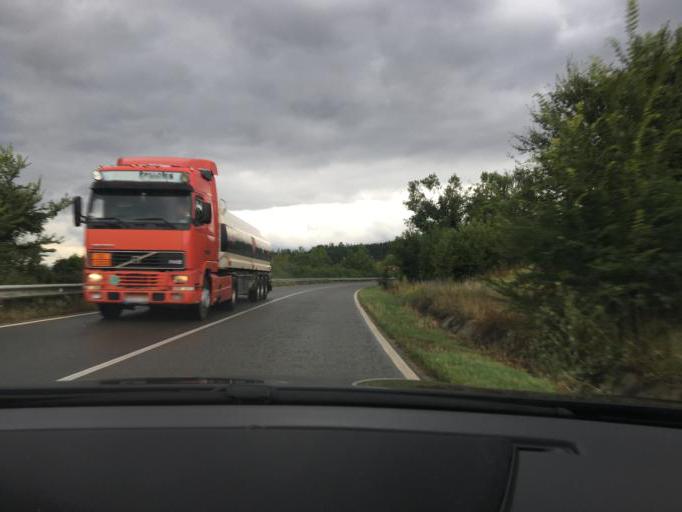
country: BG
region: Kyustendil
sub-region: Obshtina Boboshevo
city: Boboshevo
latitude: 42.2518
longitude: 22.8871
